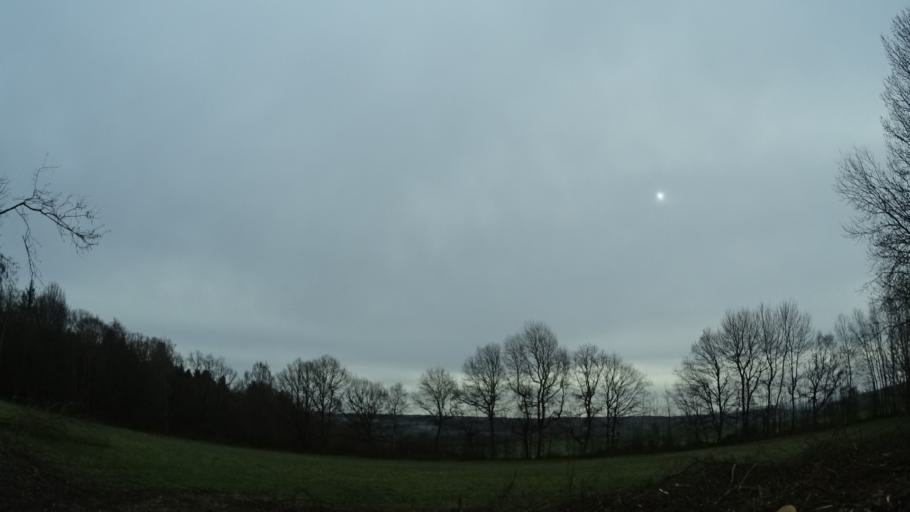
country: DE
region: Rheinland-Pfalz
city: Ippenschied
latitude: 49.8760
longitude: 7.6171
